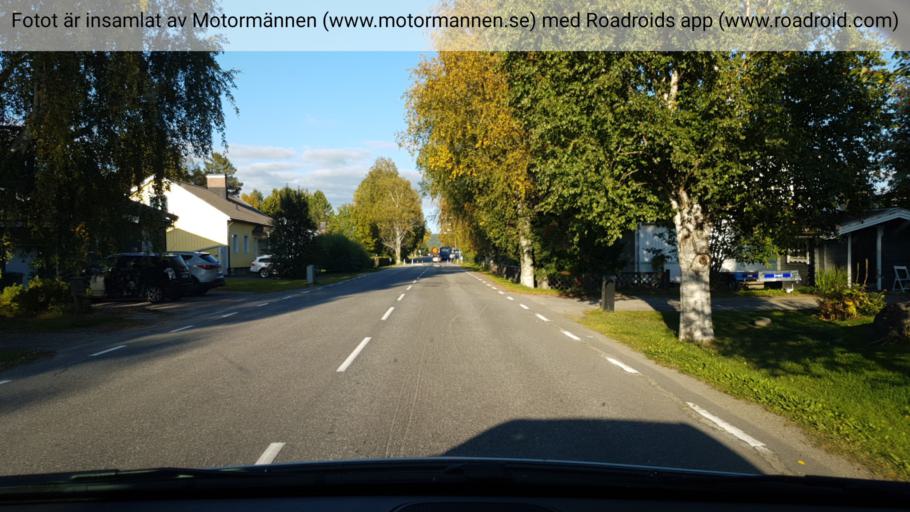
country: SE
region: Vaesterbotten
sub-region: Vannas Kommun
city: Vannasby
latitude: 63.9137
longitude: 19.8324
